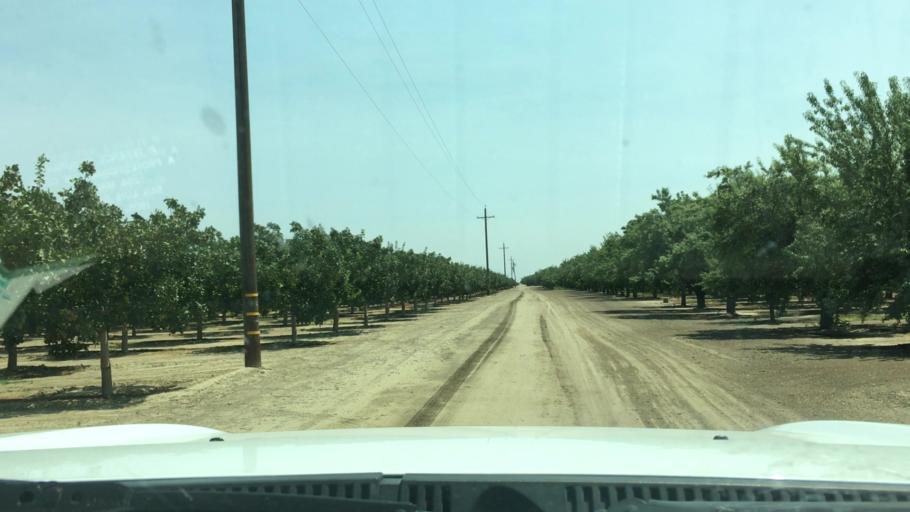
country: US
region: California
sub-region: Kern County
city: Wasco
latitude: 35.6740
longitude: -119.4338
